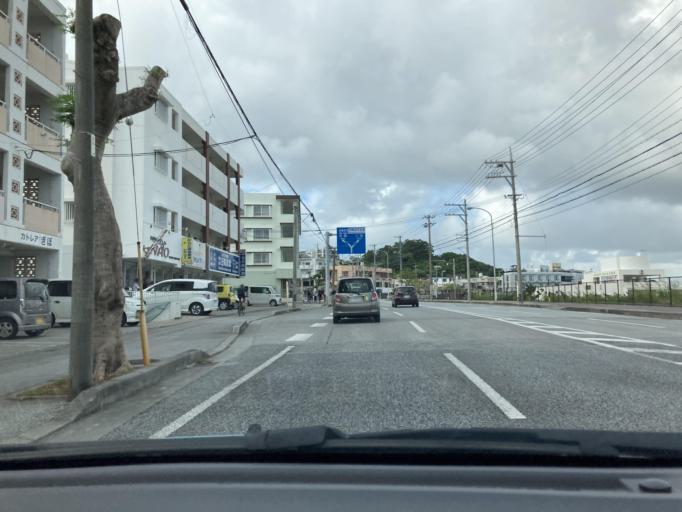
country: JP
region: Okinawa
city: Tomigusuku
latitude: 26.1803
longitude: 127.6811
